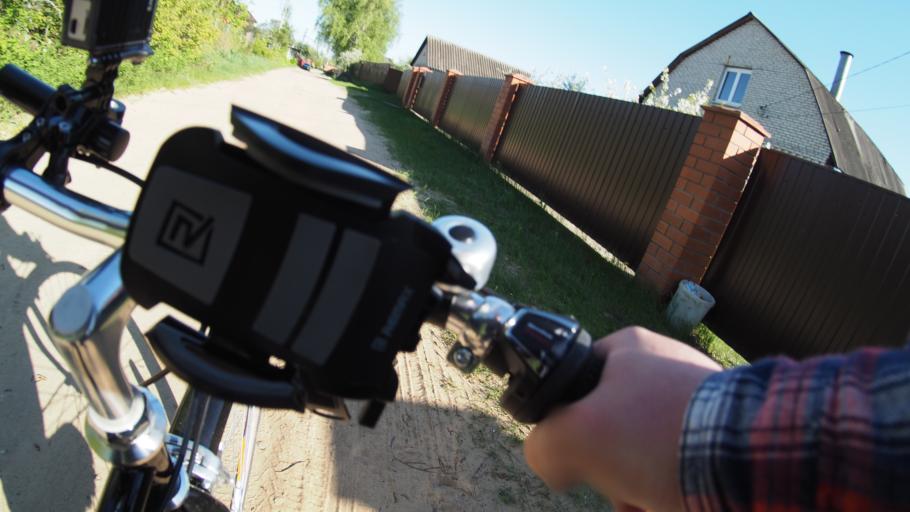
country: RU
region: Moskovskaya
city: Ramenskoye
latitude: 55.5517
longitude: 38.1899
